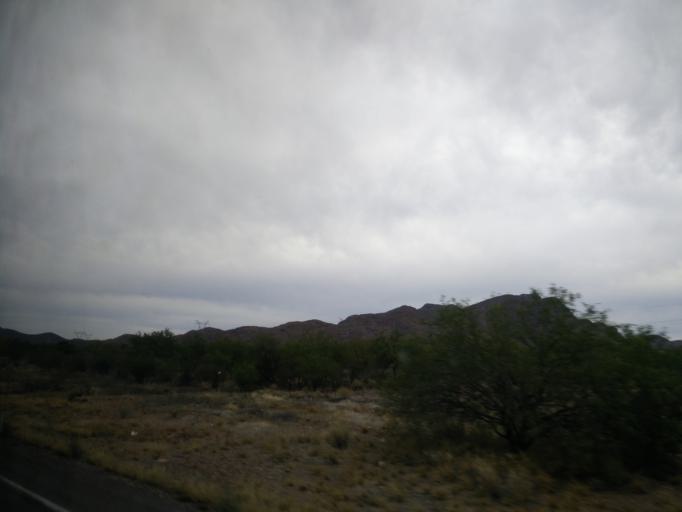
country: MX
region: Sonora
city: Hermosillo
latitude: 28.5900
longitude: -111.0246
